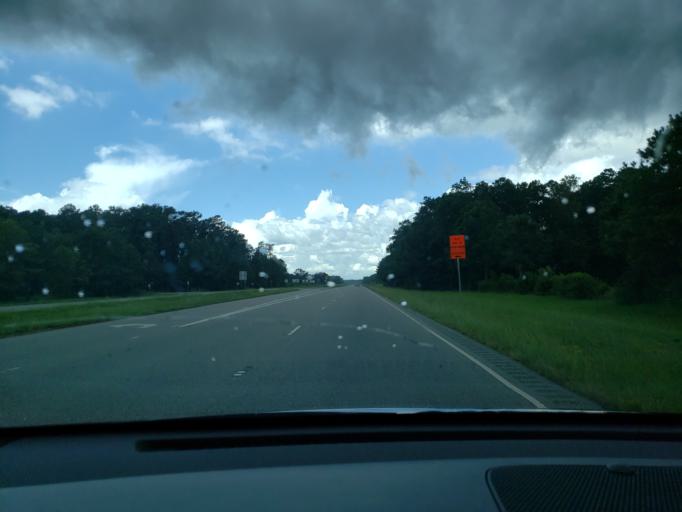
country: US
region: North Carolina
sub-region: Bladen County
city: Elizabethtown
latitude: 34.6158
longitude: -78.6430
